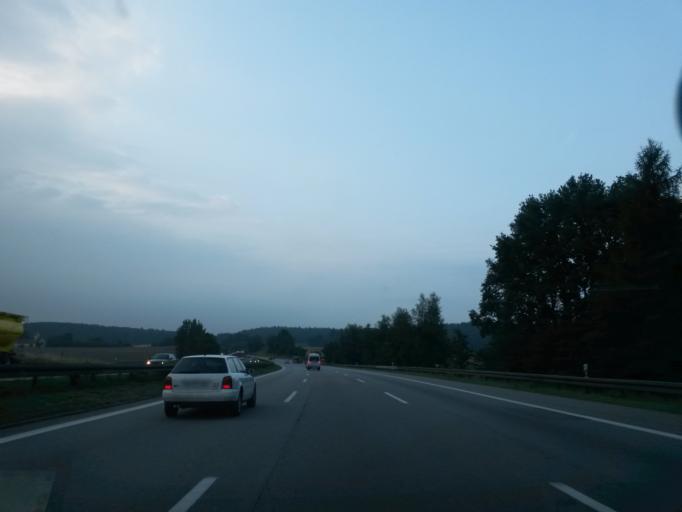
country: DE
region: Bavaria
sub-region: Upper Bavaria
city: Rohrbach
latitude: 48.6203
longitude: 11.5281
